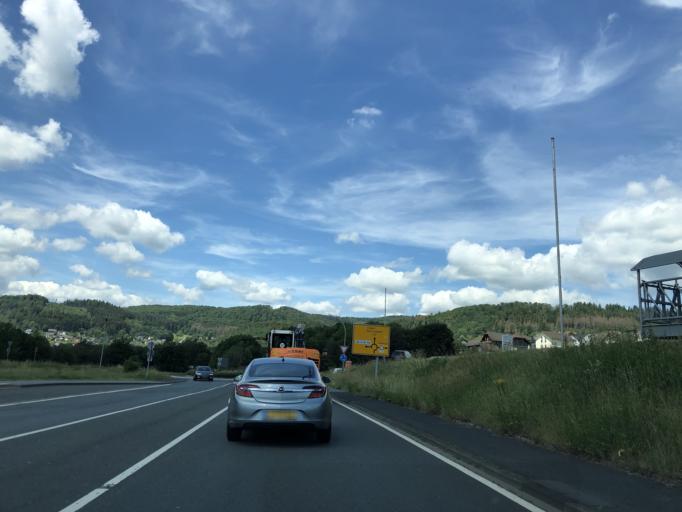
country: DE
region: North Rhine-Westphalia
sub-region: Regierungsbezirk Arnsberg
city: Bad Laasphe
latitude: 50.9293
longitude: 8.4350
